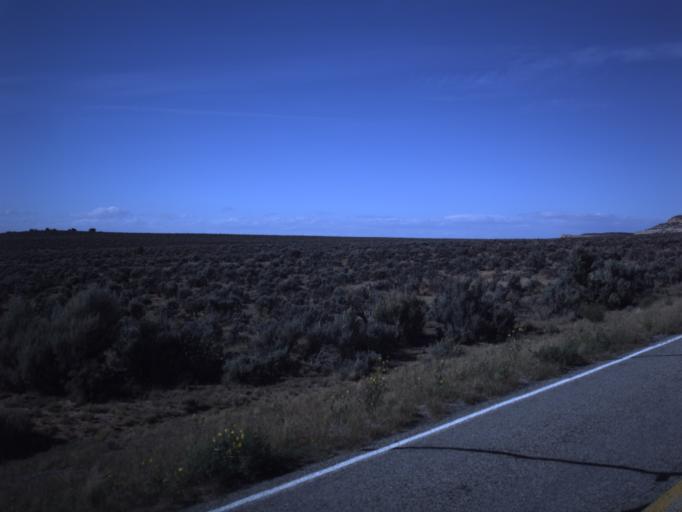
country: US
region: Utah
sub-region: San Juan County
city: Monticello
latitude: 38.0392
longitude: -109.4154
